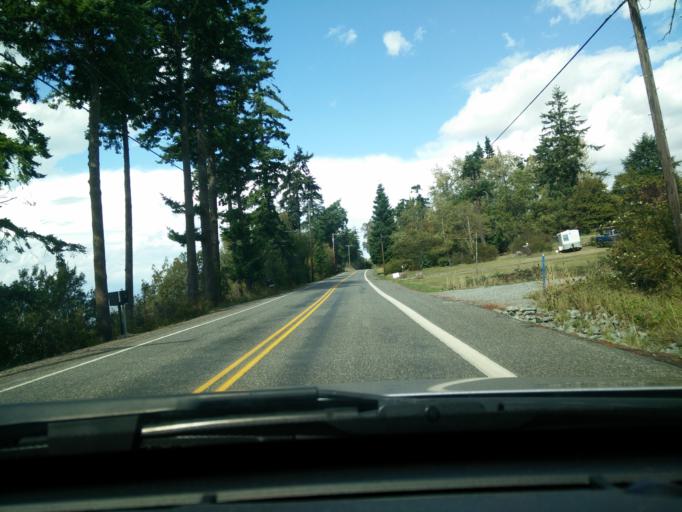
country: US
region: Washington
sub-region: Skagit County
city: Anacortes
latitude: 48.4899
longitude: -122.4815
